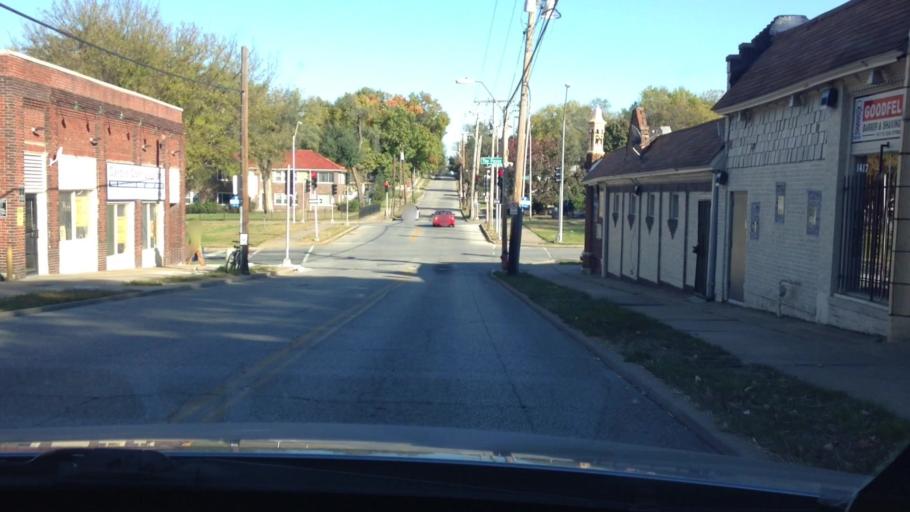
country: US
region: Kansas
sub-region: Johnson County
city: Mission Hills
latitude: 39.0270
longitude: -94.5686
